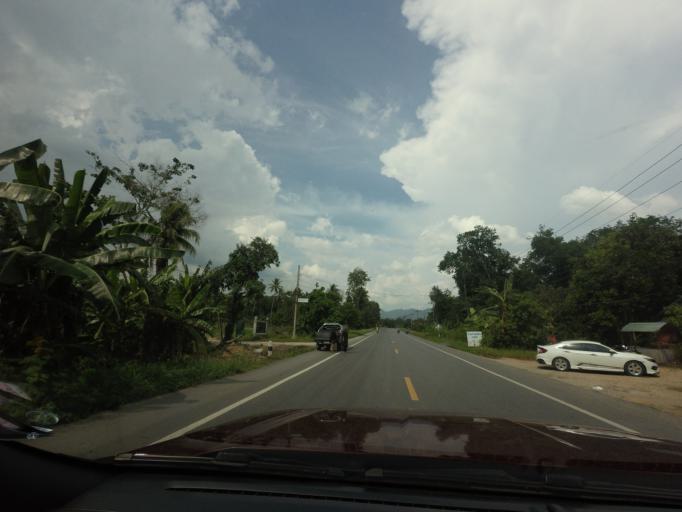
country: TH
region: Yala
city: Ban Nang Sata
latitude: 6.2569
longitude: 101.2409
